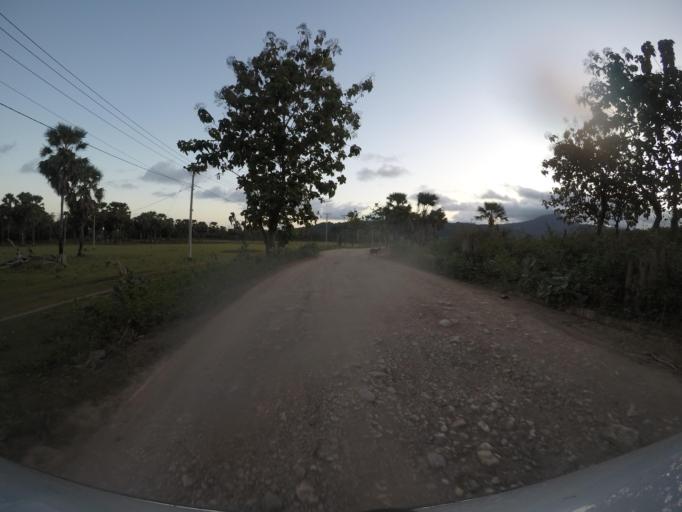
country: TL
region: Viqueque
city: Viqueque
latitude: -8.7701
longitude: 126.6427
